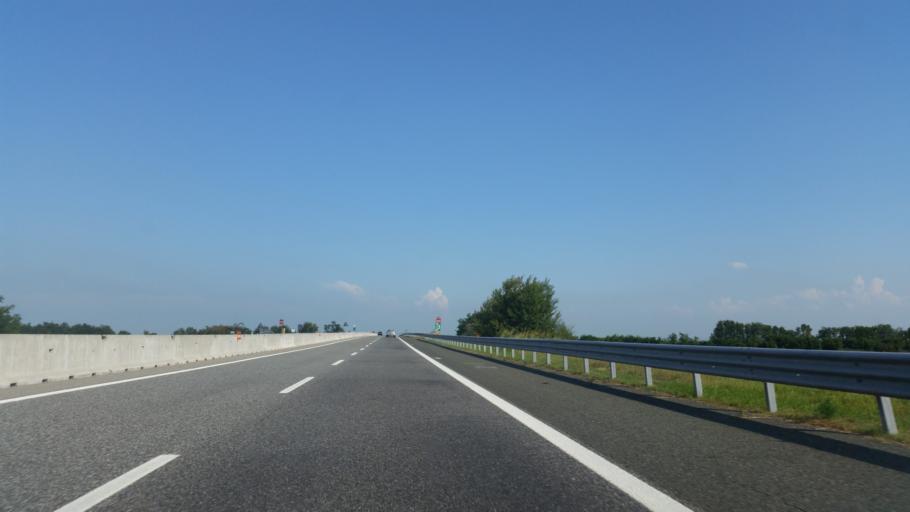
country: IT
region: Piedmont
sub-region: Provincia di Vercelli
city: Crova
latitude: 45.3405
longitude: 8.2116
